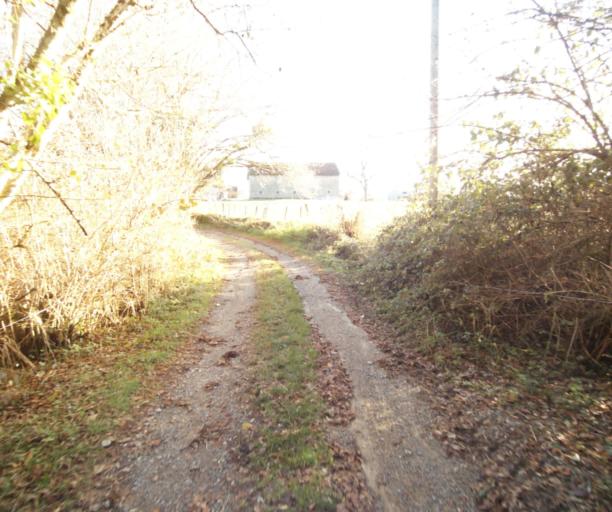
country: FR
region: Limousin
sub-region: Departement de la Correze
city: Sainte-Fortunade
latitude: 45.1881
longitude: 1.8050
